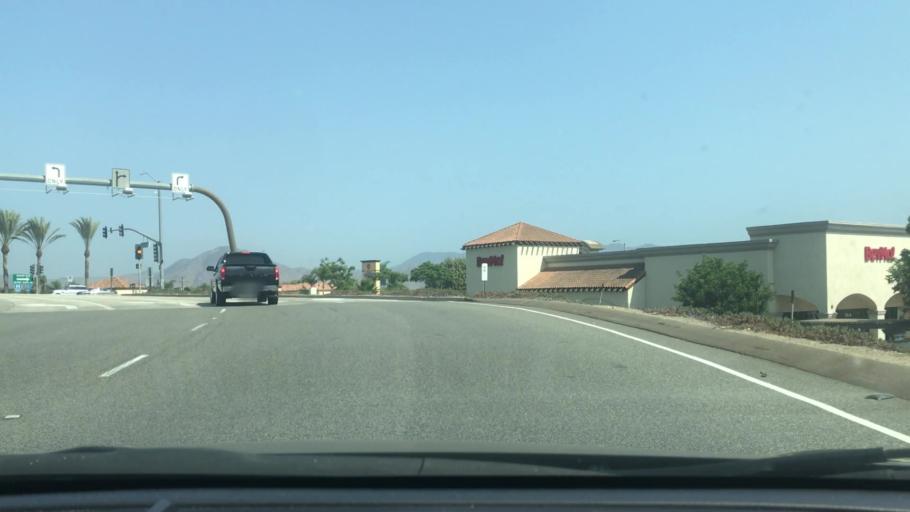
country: US
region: California
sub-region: Ventura County
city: Camarillo
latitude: 34.2179
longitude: -119.0708
